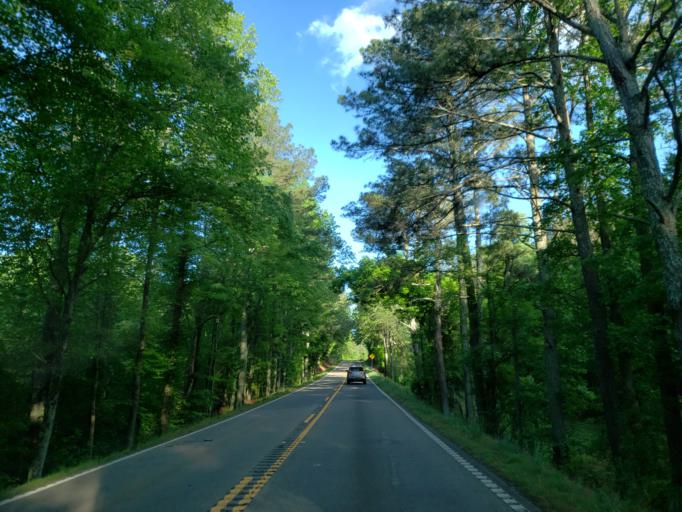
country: US
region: Georgia
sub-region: Cherokee County
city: Canton
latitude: 34.3379
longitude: -84.5702
